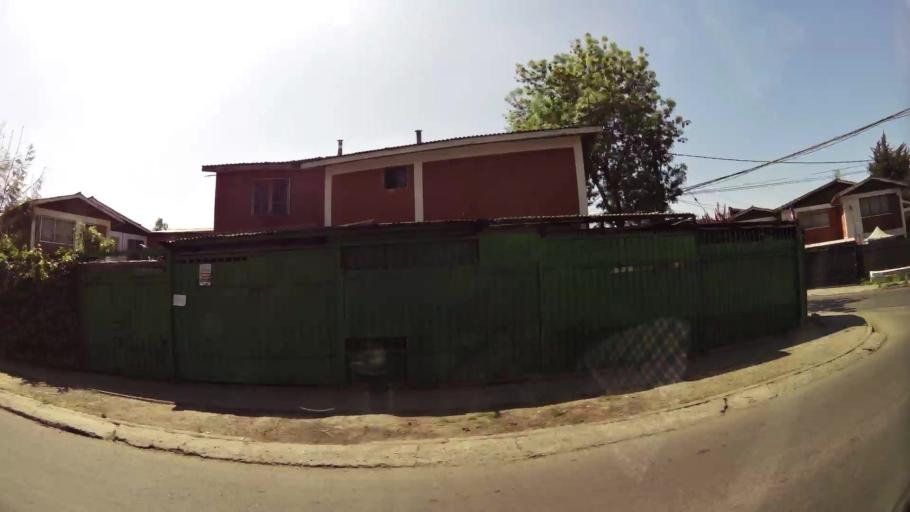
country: CL
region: Santiago Metropolitan
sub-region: Provincia de Santiago
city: Lo Prado
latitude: -33.3673
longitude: -70.7244
